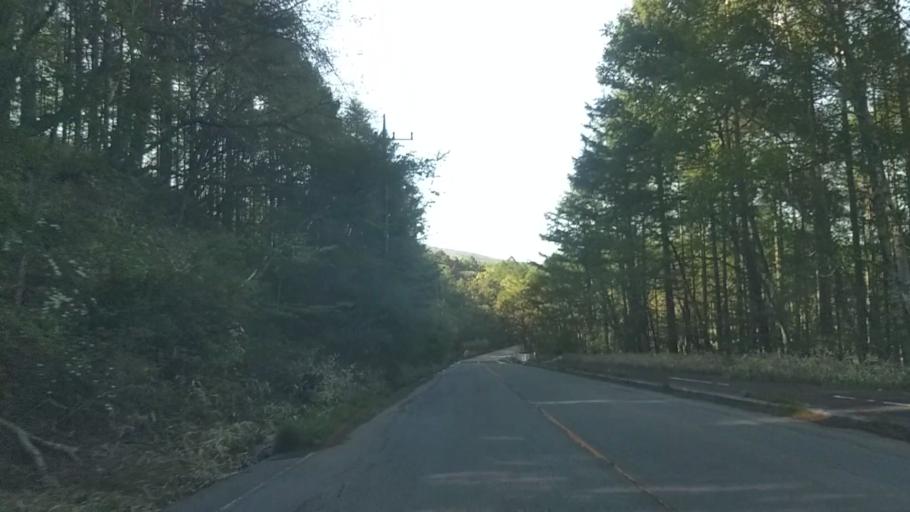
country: JP
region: Yamanashi
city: Nirasaki
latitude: 35.9136
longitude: 138.4039
